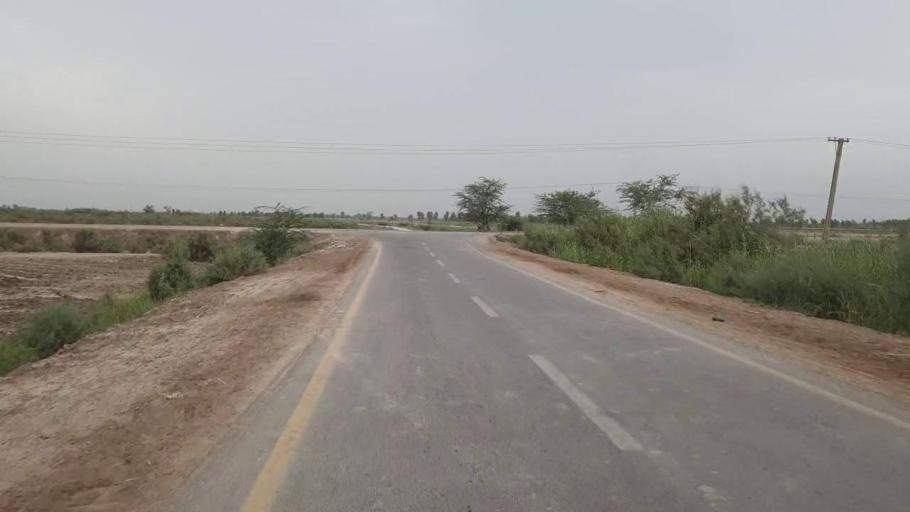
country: PK
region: Sindh
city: Bandhi
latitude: 26.5901
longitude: 68.1961
